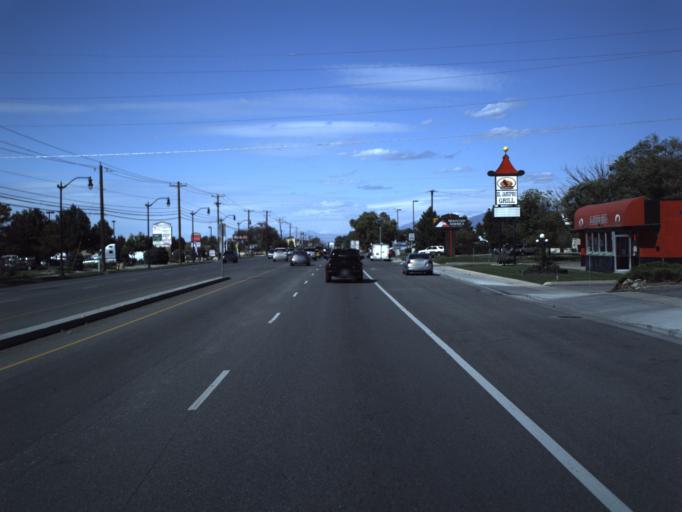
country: US
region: Utah
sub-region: Salt Lake County
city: Salt Lake City
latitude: 40.7414
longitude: -111.9390
